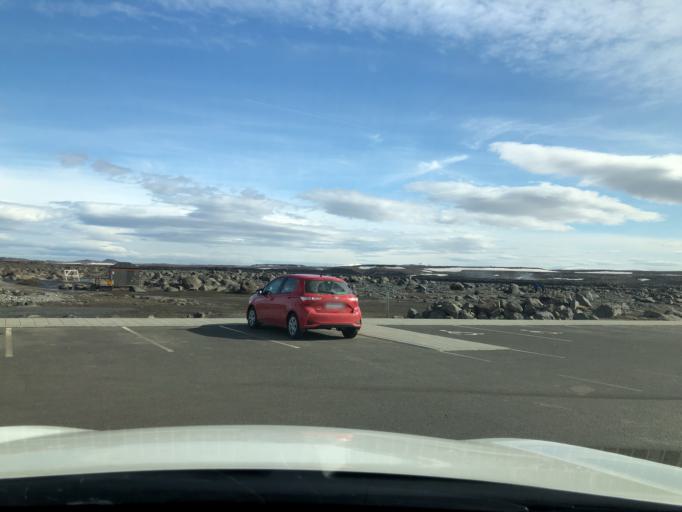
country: IS
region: Northeast
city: Husavik
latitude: 65.8116
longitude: -16.4003
